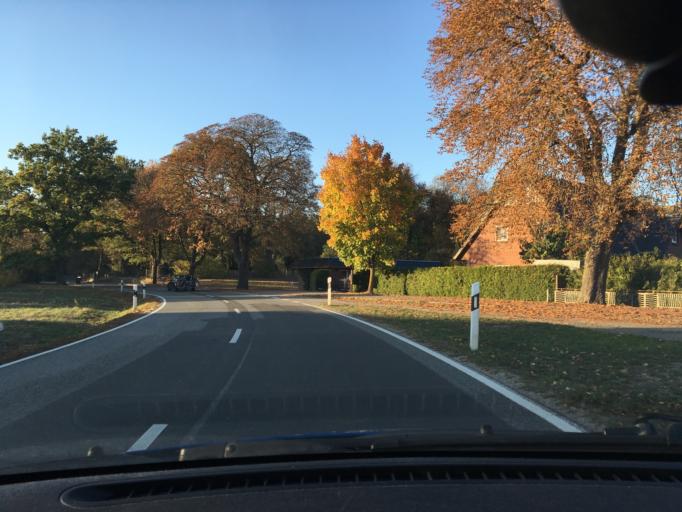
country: DE
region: Mecklenburg-Vorpommern
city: Boizenburg
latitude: 53.3519
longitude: 10.8073
